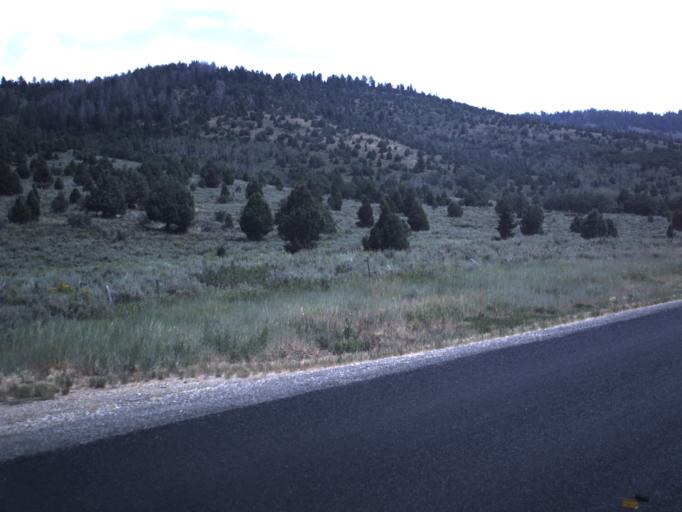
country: US
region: Utah
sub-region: Summit County
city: Francis
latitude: 40.5580
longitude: -111.1162
